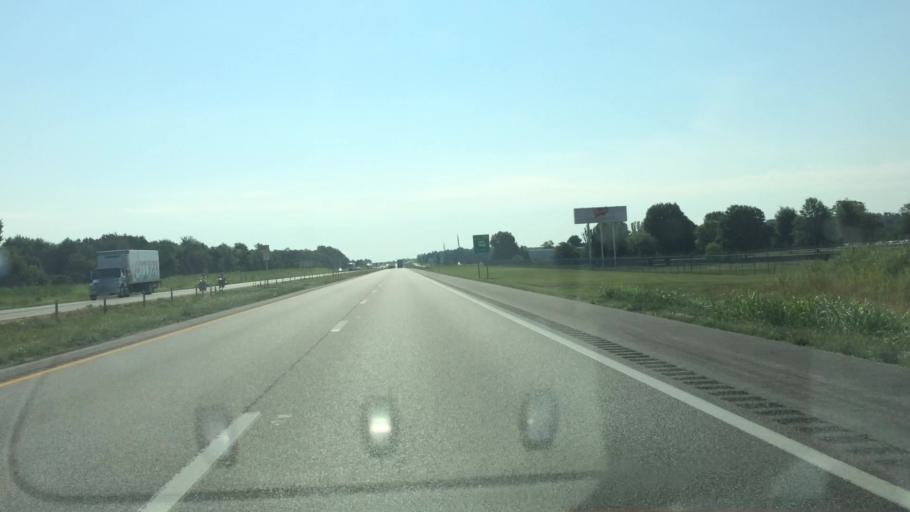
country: US
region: Missouri
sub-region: Greene County
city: Strafford
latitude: 37.2502
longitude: -93.2062
